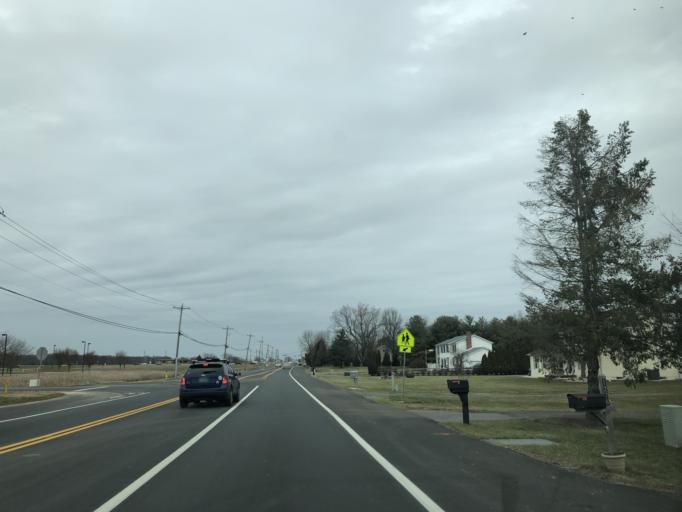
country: US
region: Delaware
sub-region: New Castle County
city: Middletown
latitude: 39.4994
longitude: -75.6862
